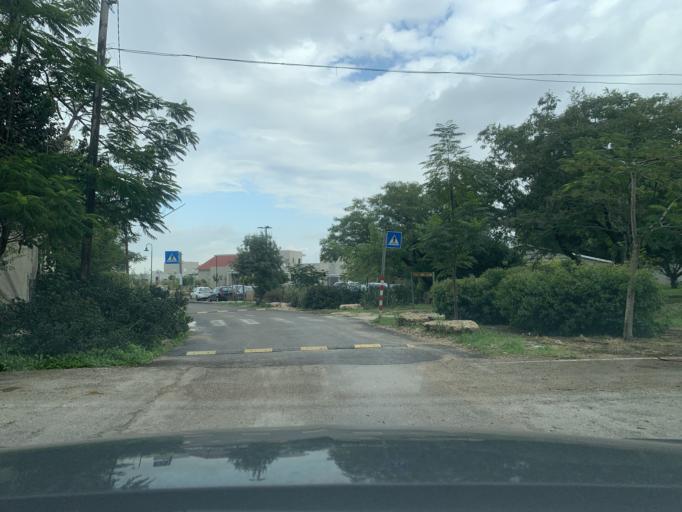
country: PS
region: West Bank
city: Qalqilyah
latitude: 32.2120
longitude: 34.9767
